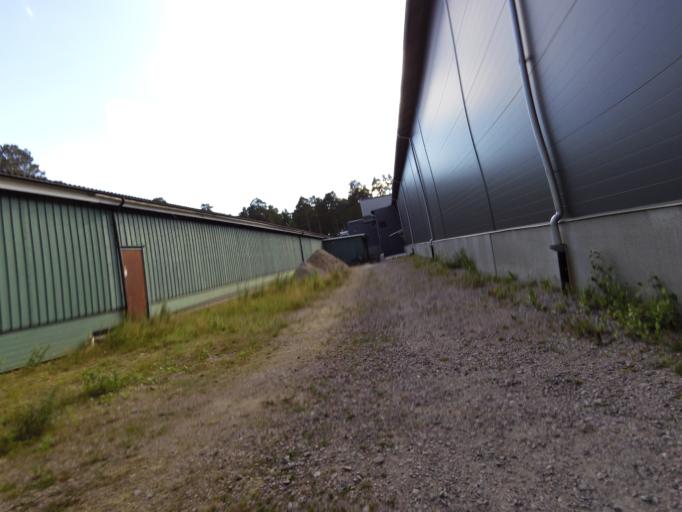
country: SE
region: Gaevleborg
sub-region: Gavle Kommun
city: Gavle
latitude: 60.7084
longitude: 17.1651
